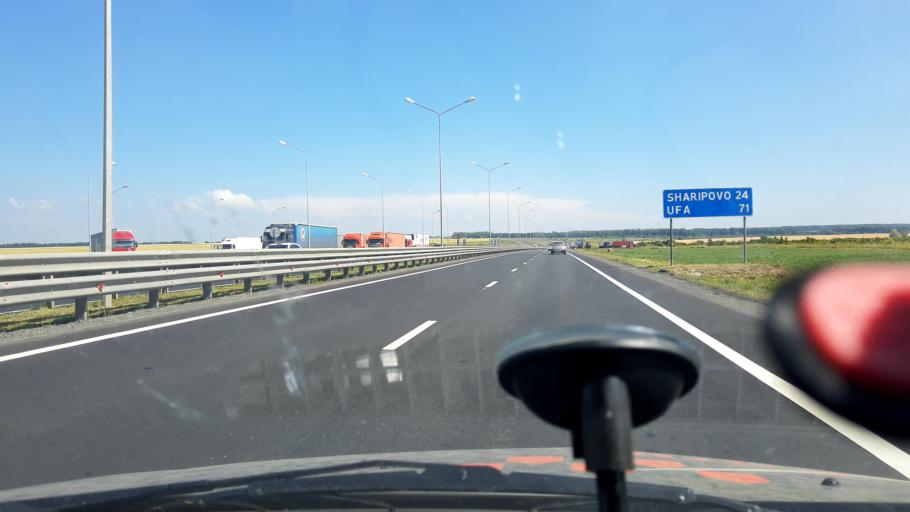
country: RU
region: Bashkortostan
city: Kushnarenkovo
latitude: 55.0737
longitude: 55.2857
